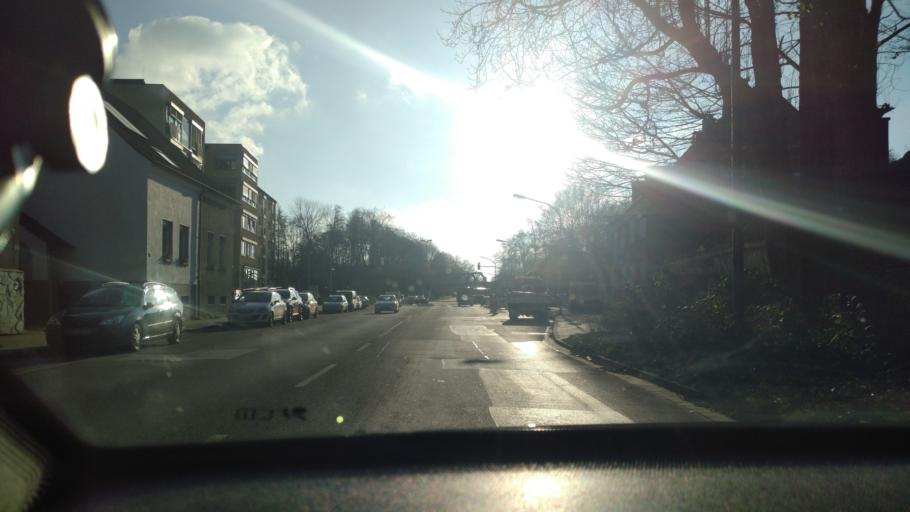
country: DE
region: North Rhine-Westphalia
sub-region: Regierungsbezirk Dusseldorf
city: Essen
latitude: 51.4900
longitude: 6.9804
